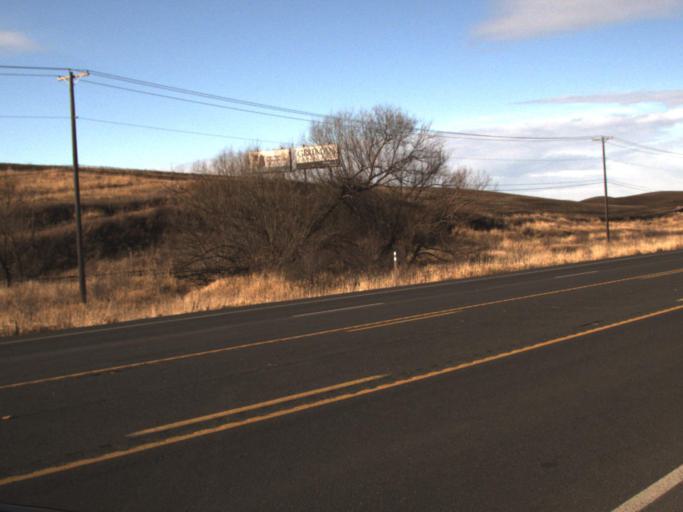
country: US
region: Idaho
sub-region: Latah County
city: Moscow
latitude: 46.7370
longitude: -117.0518
